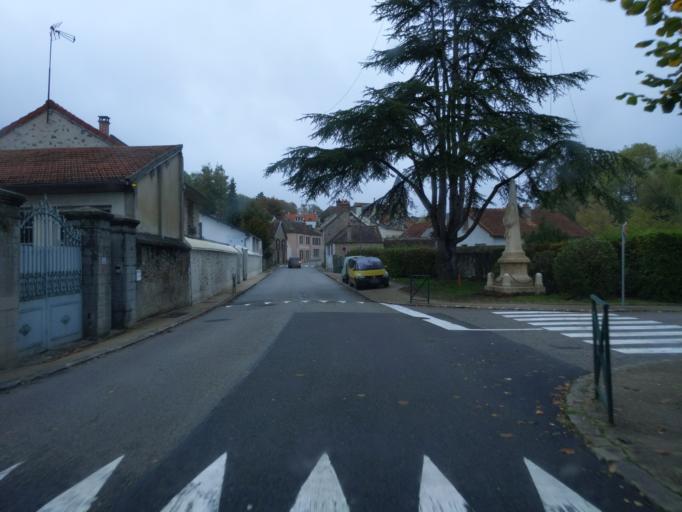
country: FR
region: Ile-de-France
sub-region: Departement des Yvelines
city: Dampierre-en-Yvelines
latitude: 48.7034
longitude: 1.9841
